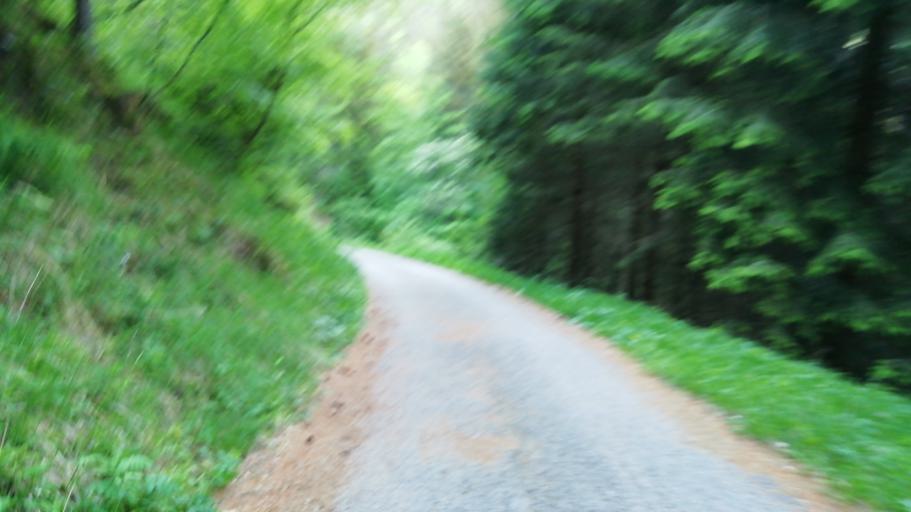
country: IT
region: Veneto
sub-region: Provincia di Belluno
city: Valle di Cadore
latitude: 46.4257
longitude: 12.3221
